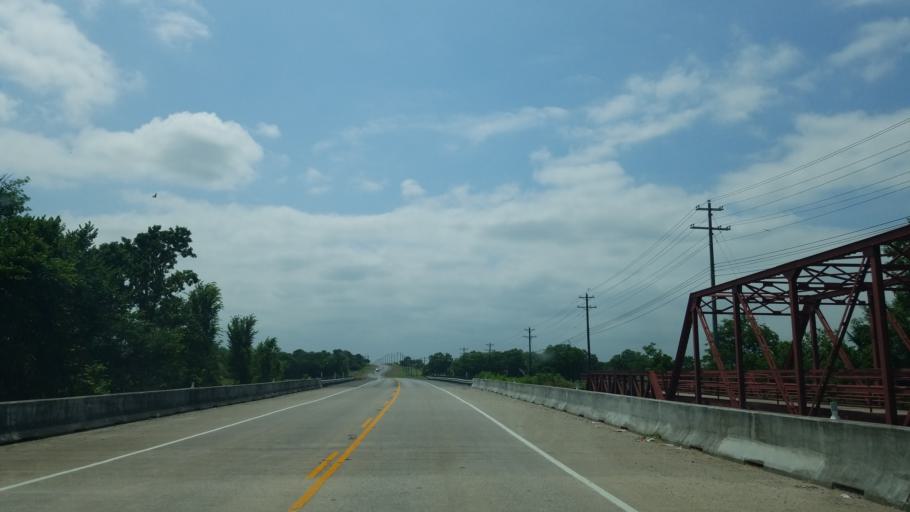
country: US
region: Texas
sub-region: Denton County
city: Aubrey
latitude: 33.3067
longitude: -97.0420
